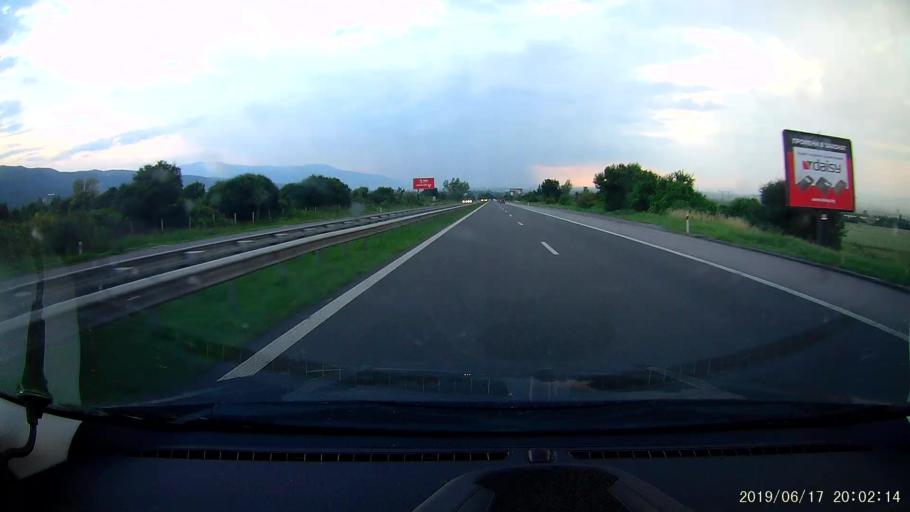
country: BG
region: Sofiya
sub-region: Obshtina Elin Pelin
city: Elin Pelin
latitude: 42.6115
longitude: 23.5391
